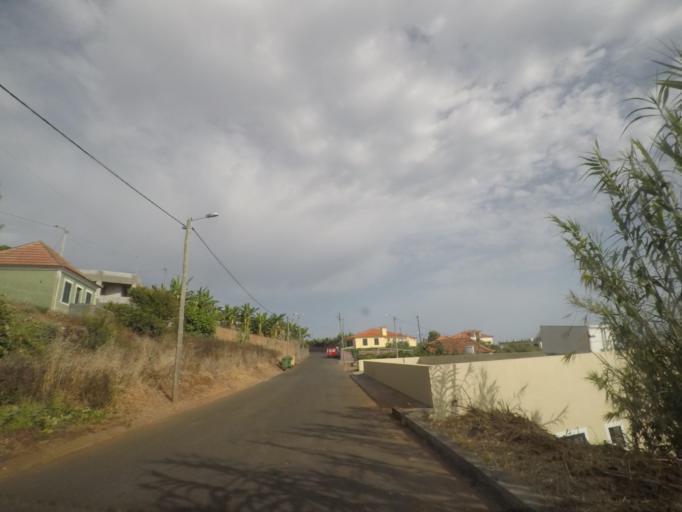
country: PT
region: Madeira
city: Ponta do Sol
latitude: 32.6940
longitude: -17.1182
